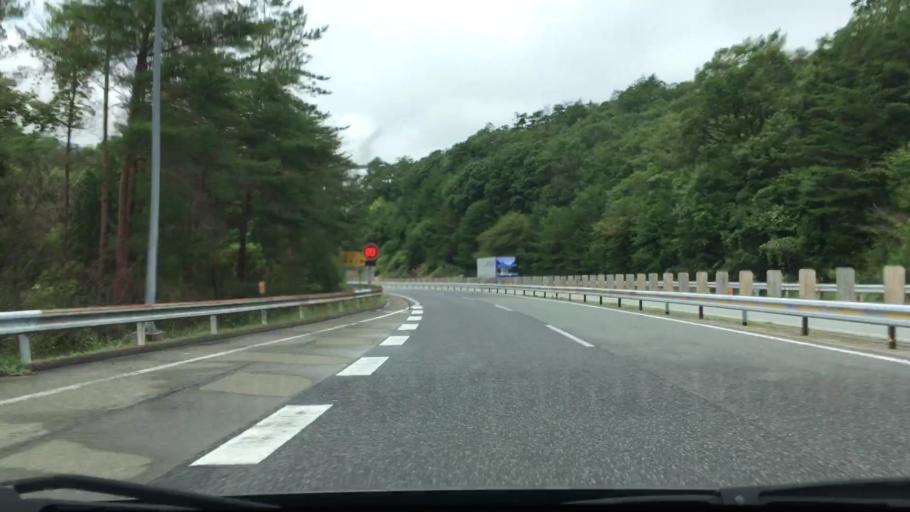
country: JP
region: Hiroshima
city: Shobara
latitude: 34.8608
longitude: 133.1020
